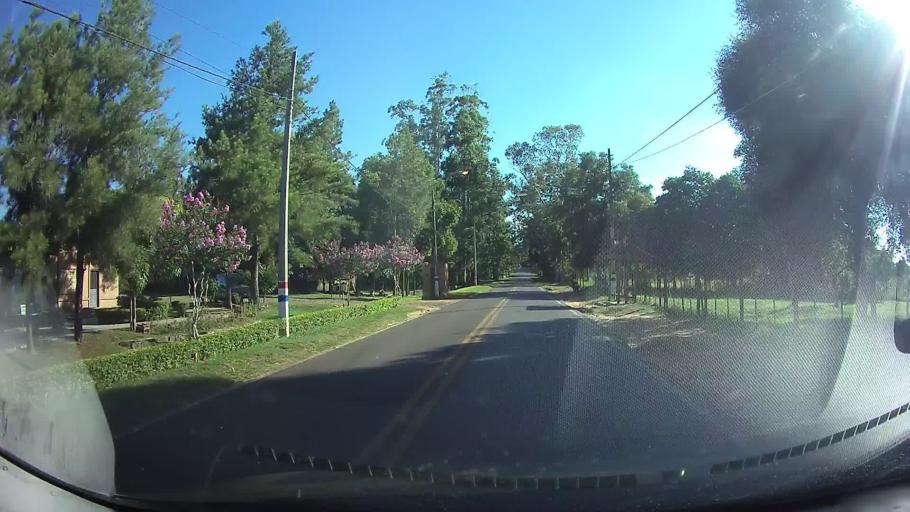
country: PY
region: Cordillera
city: Atyra
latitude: -25.2856
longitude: -57.1774
